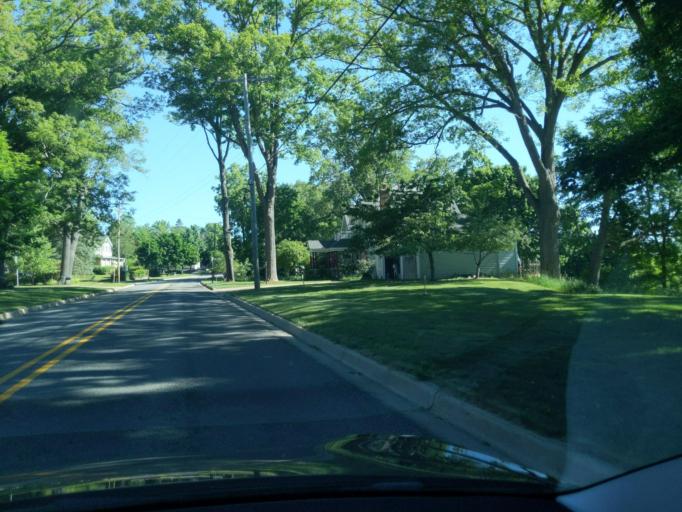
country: US
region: Michigan
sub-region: Muskegon County
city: Montague
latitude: 43.4104
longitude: -86.3604
